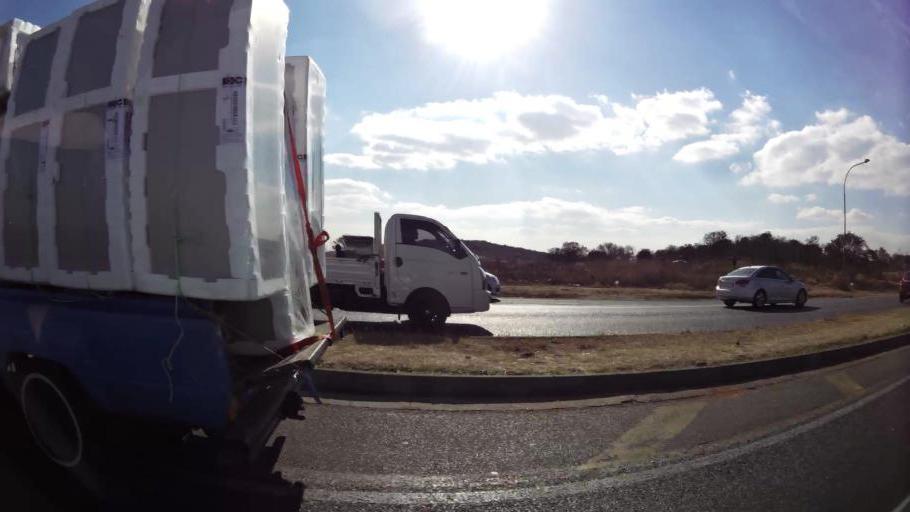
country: ZA
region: Gauteng
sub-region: City of Johannesburg Metropolitan Municipality
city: Soweto
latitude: -26.2860
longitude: 27.9273
